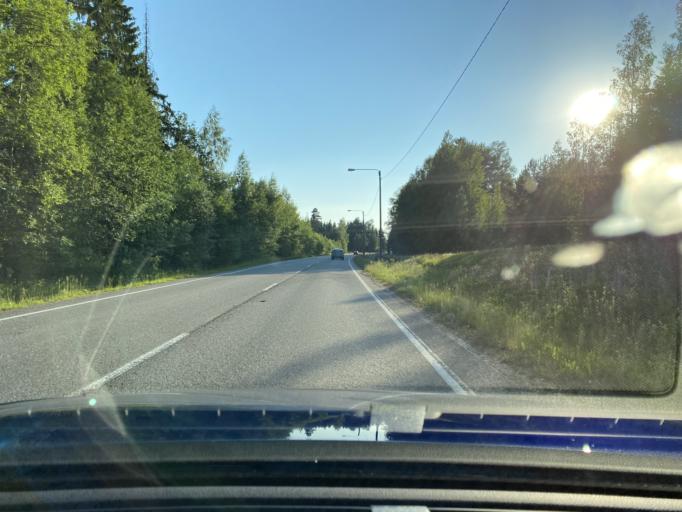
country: FI
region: Haeme
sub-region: Riihimaeki
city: Riihimaeki
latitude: 60.7173
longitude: 24.7185
